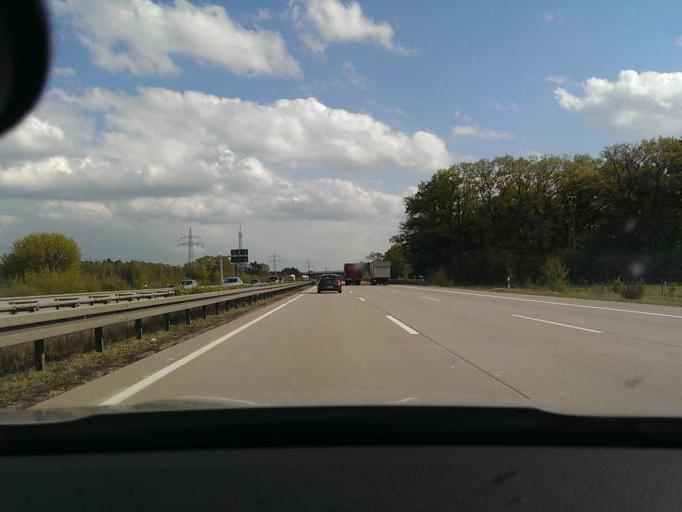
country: DE
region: Lower Saxony
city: Isernhagen Farster Bauerschaft
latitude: 52.5370
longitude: 9.8043
